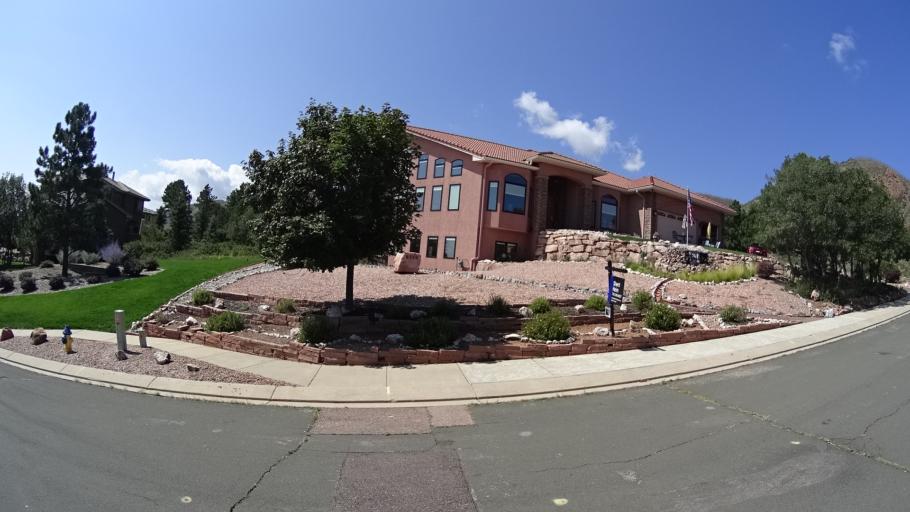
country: US
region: Colorado
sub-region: El Paso County
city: Manitou Springs
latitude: 38.9225
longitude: -104.8835
